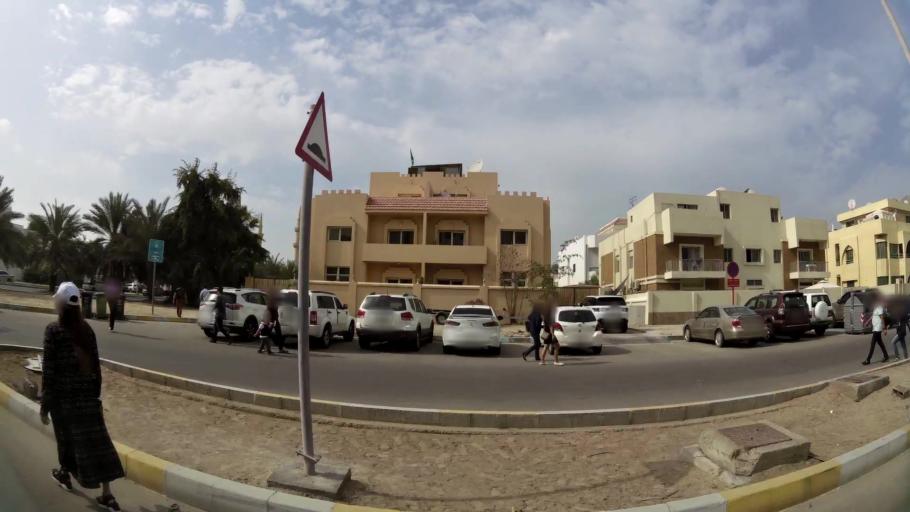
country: AE
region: Abu Dhabi
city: Abu Dhabi
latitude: 24.4518
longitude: 54.3865
